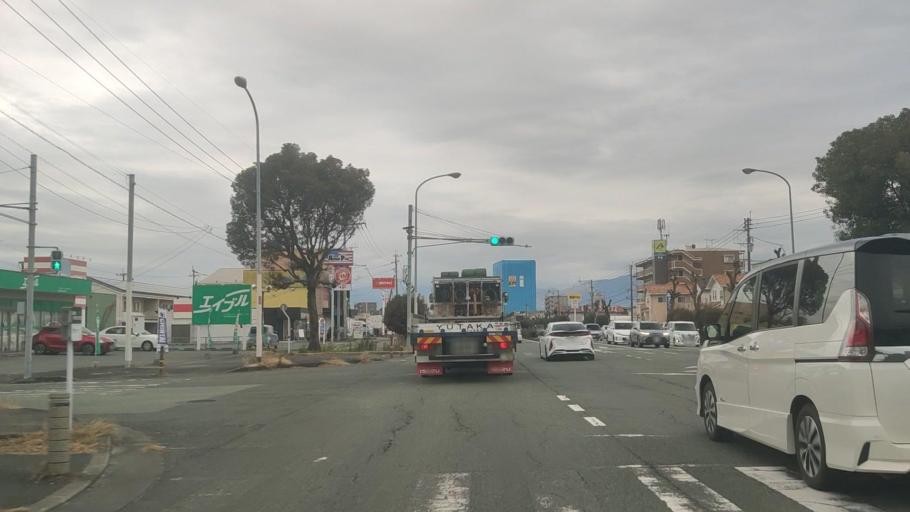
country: JP
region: Kumamoto
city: Ozu
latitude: 32.8627
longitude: 130.8180
